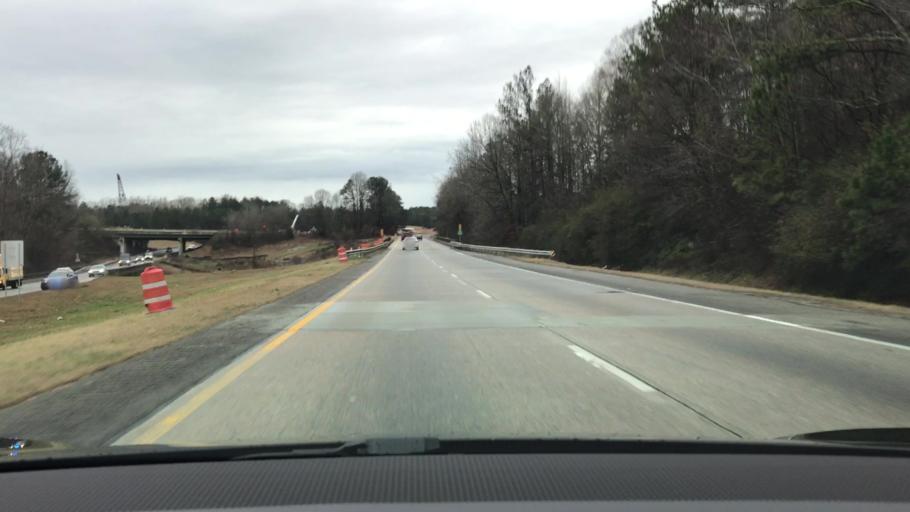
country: US
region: Georgia
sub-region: Gwinnett County
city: Suwanee
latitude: 34.0487
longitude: -84.0286
